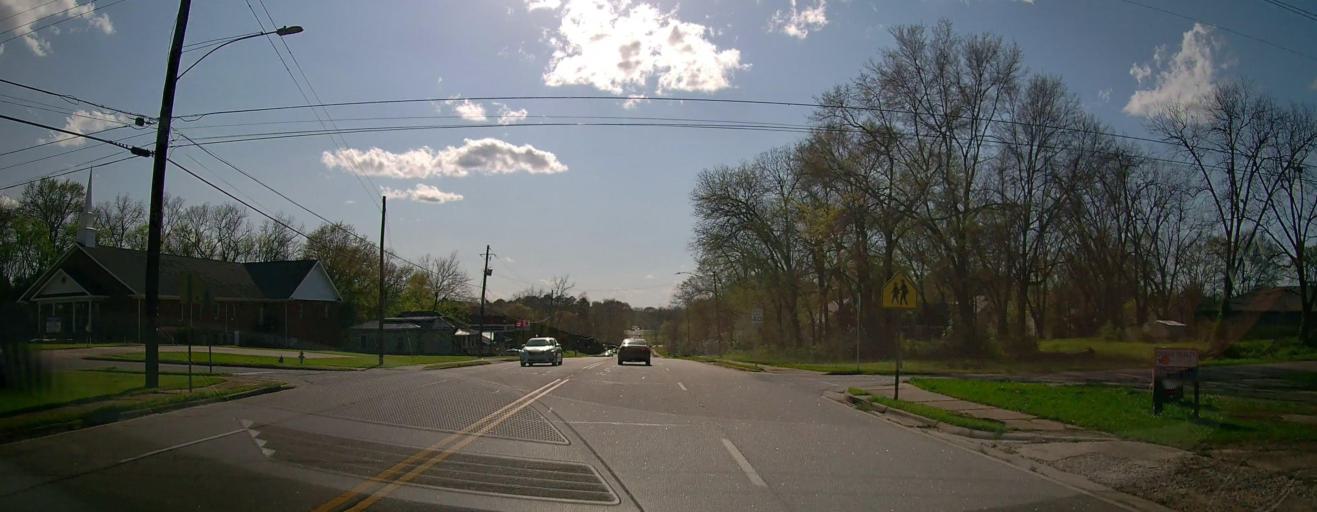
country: US
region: Georgia
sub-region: Baldwin County
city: Milledgeville
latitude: 33.0819
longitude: -83.2392
